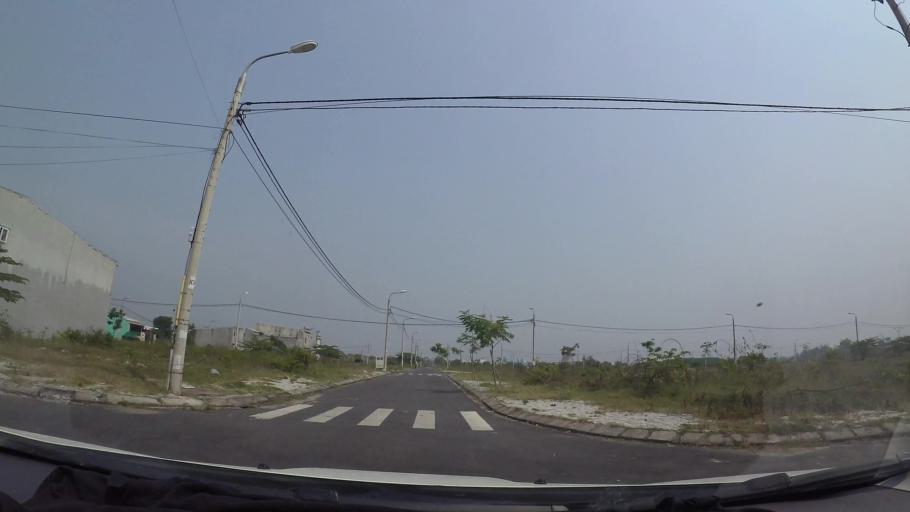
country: VN
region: Da Nang
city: Cam Le
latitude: 15.9696
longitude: 108.2135
